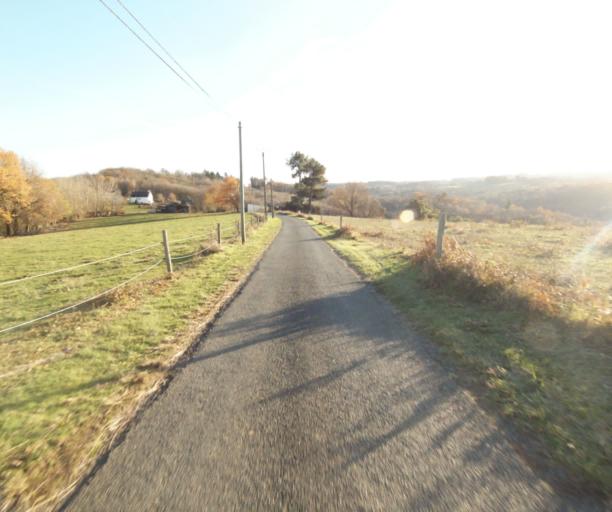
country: FR
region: Limousin
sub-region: Departement de la Correze
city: Laguenne
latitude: 45.2252
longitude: 1.8016
